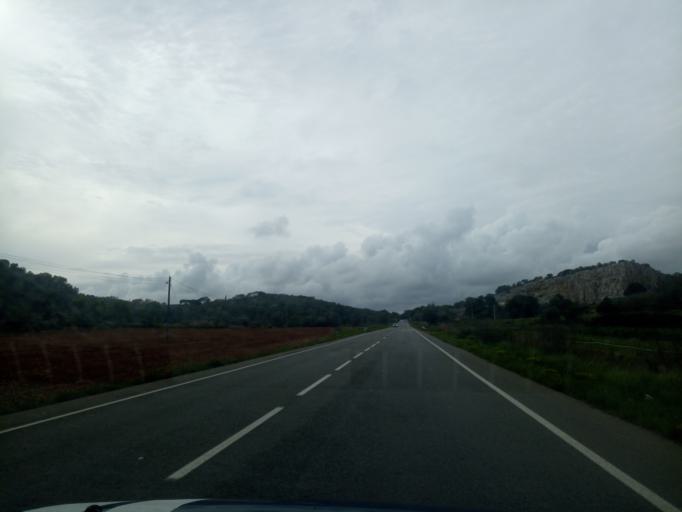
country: ES
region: Catalonia
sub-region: Provincia de Barcelona
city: Sitges
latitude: 41.2336
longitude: 1.7821
